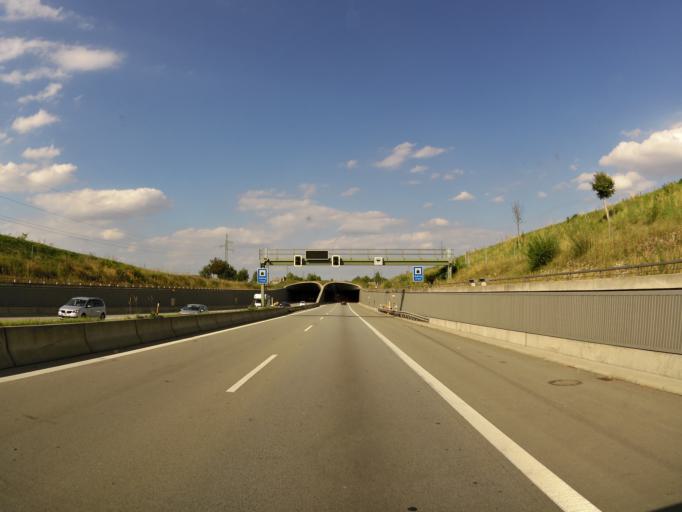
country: DE
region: Bavaria
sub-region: Upper Bavaria
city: Germering
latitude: 48.1563
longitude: 11.4004
